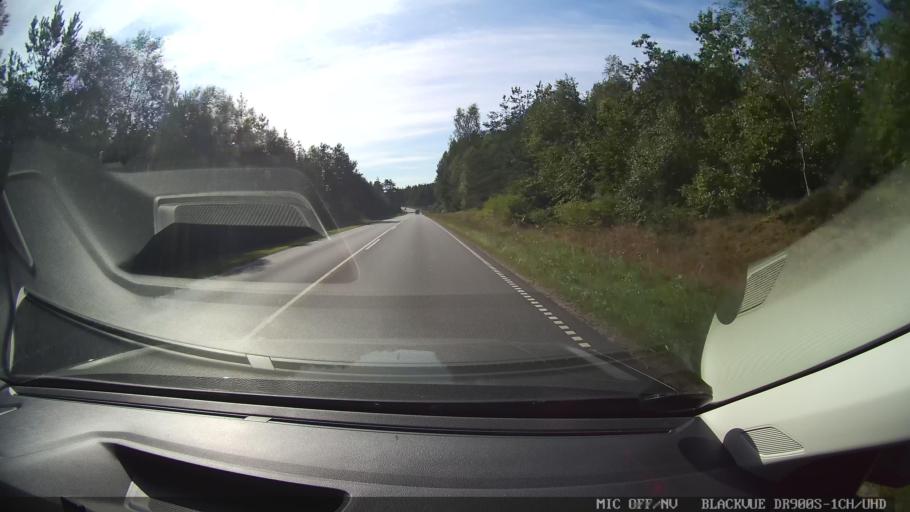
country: DK
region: North Denmark
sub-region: Mariagerfjord Kommune
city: Hadsund
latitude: 56.7372
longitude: 10.0781
